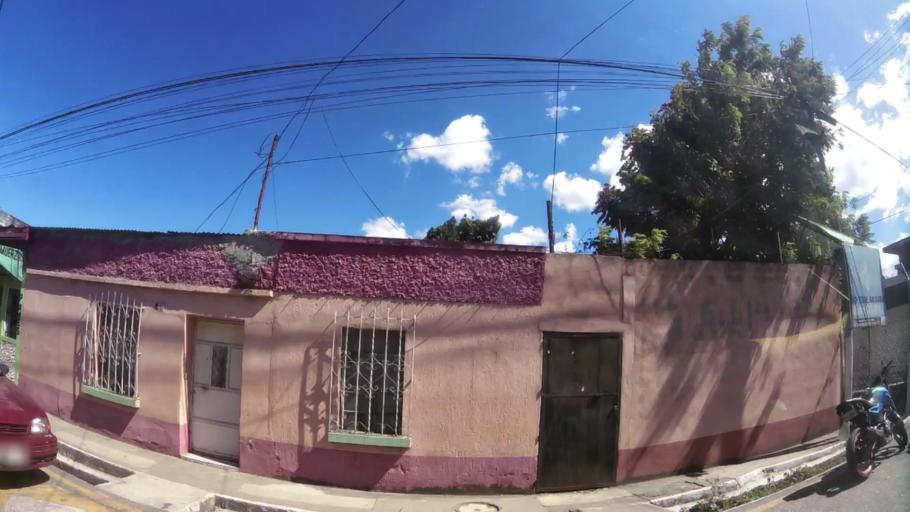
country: GT
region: Guatemala
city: Villa Canales
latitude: 14.4844
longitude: -90.5341
